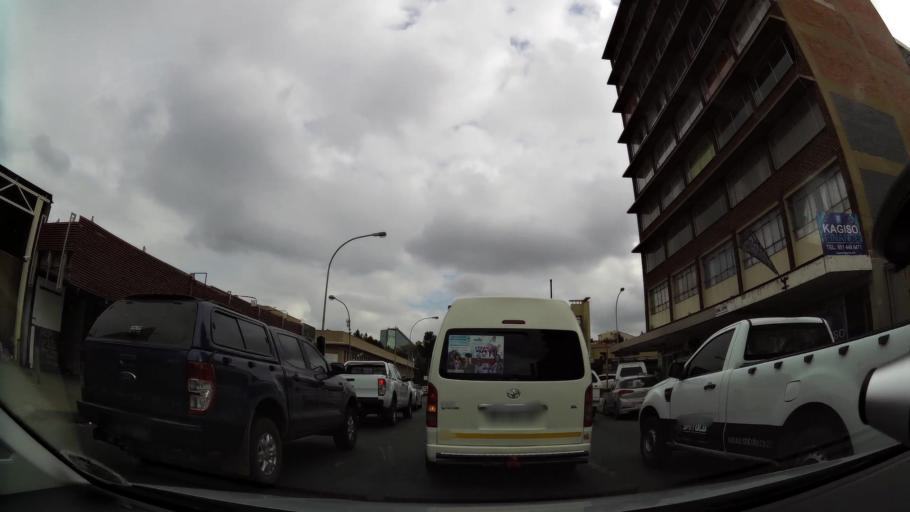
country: ZA
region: Orange Free State
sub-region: Mangaung Metropolitan Municipality
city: Bloemfontein
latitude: -29.1138
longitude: 26.2194
